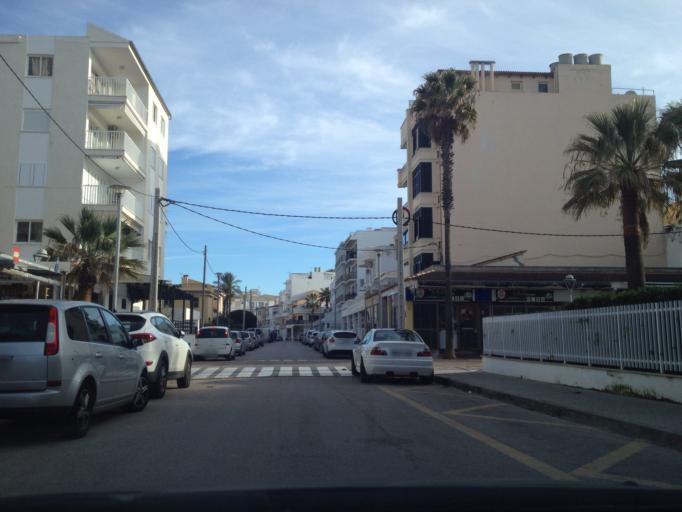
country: ES
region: Balearic Islands
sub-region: Illes Balears
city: Port d'Alcudia
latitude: 39.7690
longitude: 3.1496
